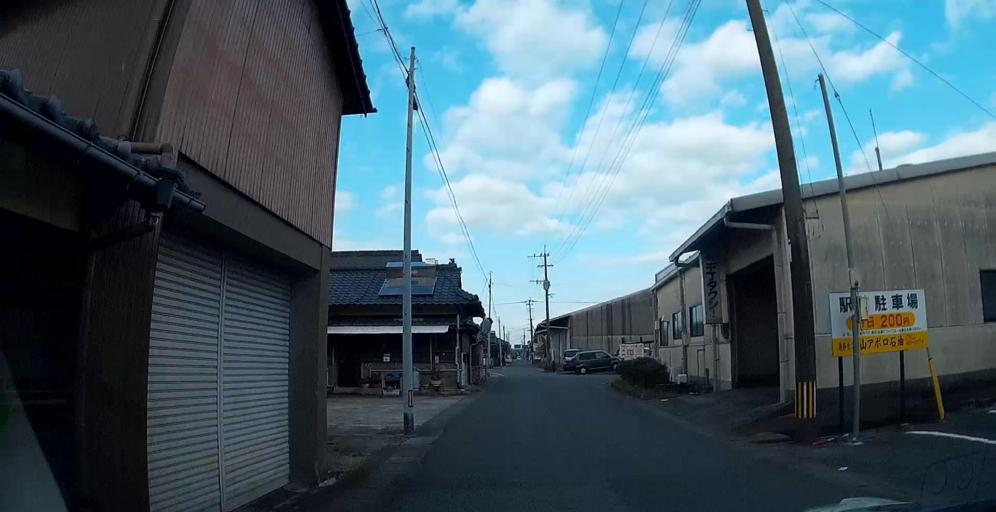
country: JP
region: Kumamoto
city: Yatsushiro
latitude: 32.5330
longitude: 130.6454
